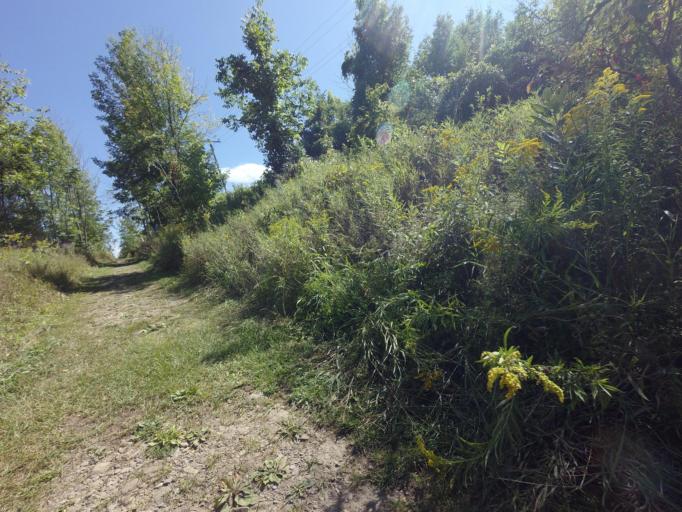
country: CA
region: Ontario
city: Orangeville
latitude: 43.8197
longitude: -80.0133
